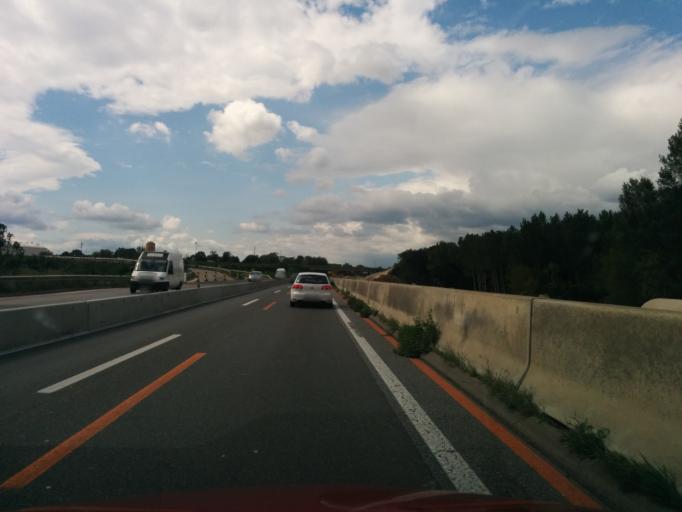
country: AT
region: Lower Austria
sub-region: Politischer Bezirk Wien-Umgebung
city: Fischamend Dorf
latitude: 48.1290
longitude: 16.5574
